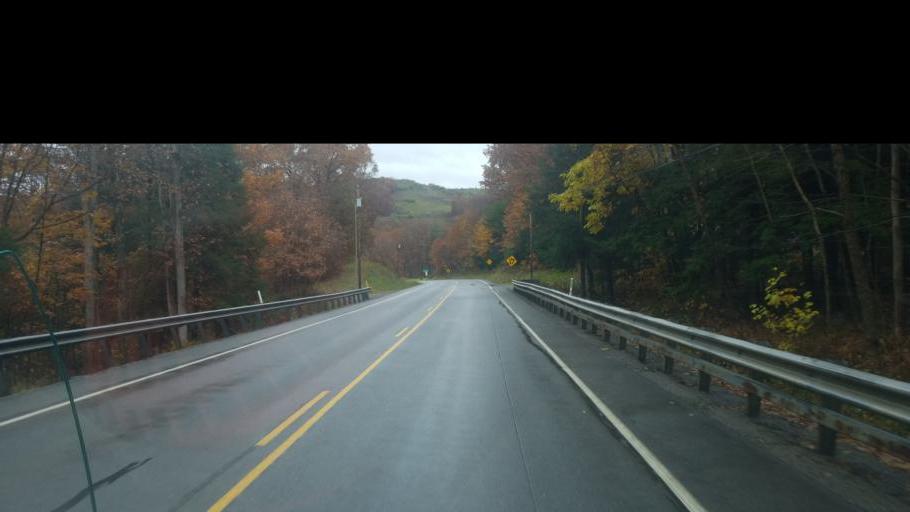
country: US
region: Pennsylvania
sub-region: Clearfield County
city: Shiloh
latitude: 41.1260
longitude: -78.1375
